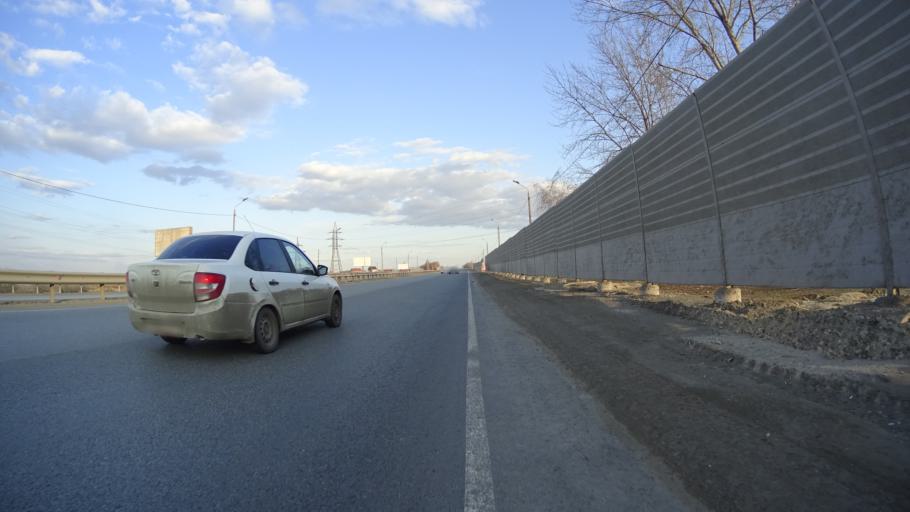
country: RU
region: Chelyabinsk
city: Novosineglazovskiy
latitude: 55.0457
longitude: 61.4195
